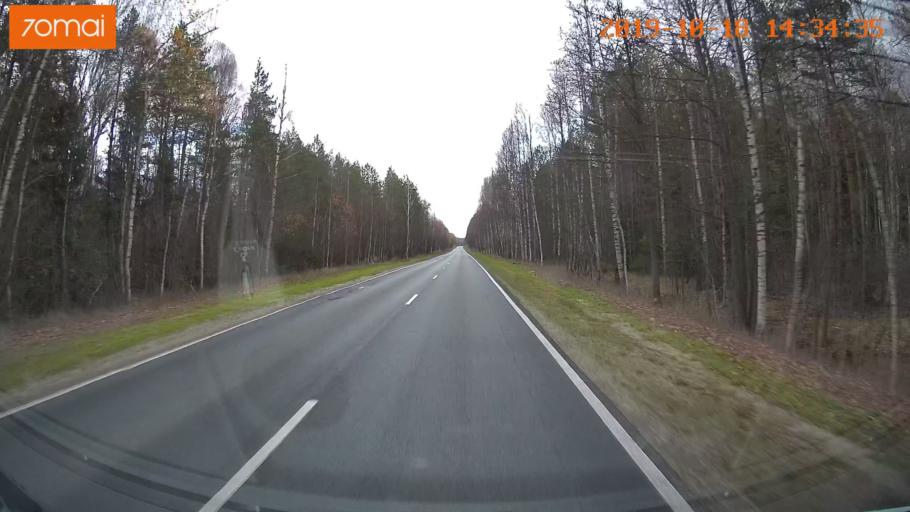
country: RU
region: Vladimir
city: Velikodvorskiy
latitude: 55.2137
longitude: 40.6190
